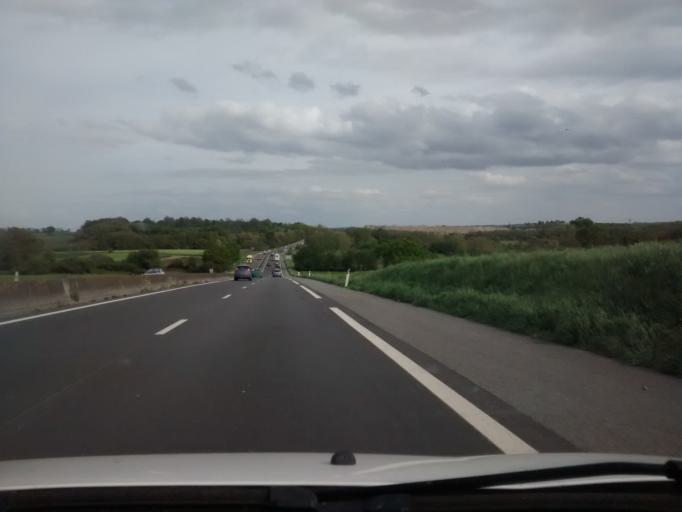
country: FR
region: Brittany
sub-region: Departement d'Ille-et-Vilaine
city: Saint-Pere
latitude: 48.5745
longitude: -1.9397
